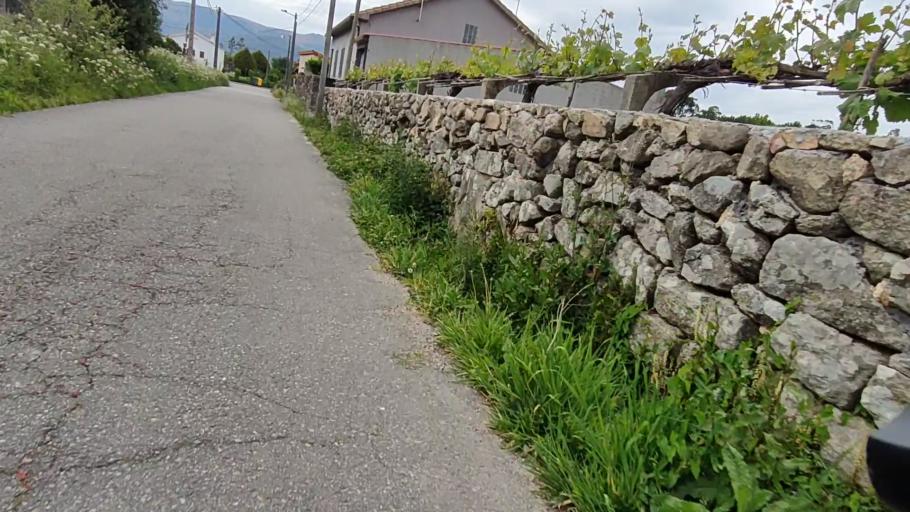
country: ES
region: Galicia
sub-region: Provincia da Coruna
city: Boiro
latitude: 42.6337
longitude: -8.8657
